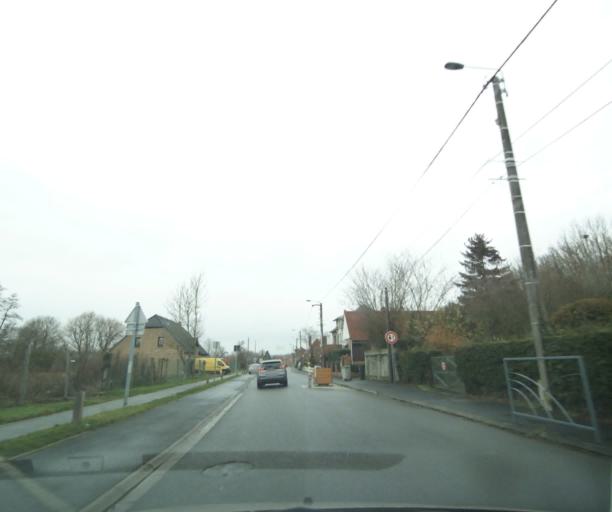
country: FR
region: Nord-Pas-de-Calais
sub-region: Departement du Nord
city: Prouvy
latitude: 50.3222
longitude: 3.4438
